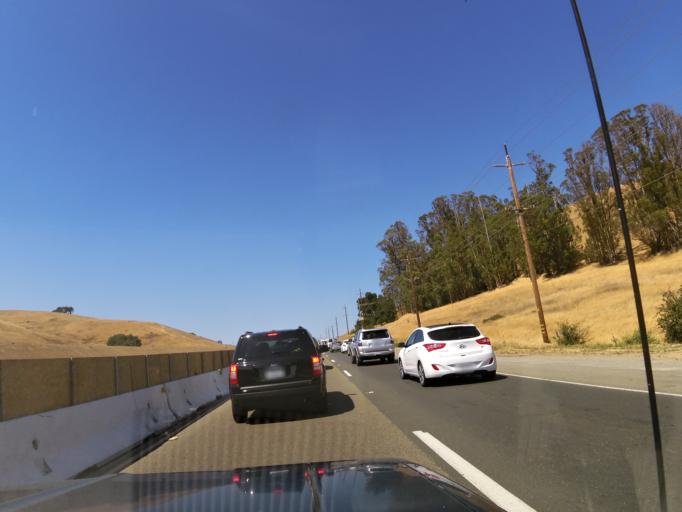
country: US
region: California
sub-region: Sonoma County
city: Petaluma
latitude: 38.1925
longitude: -122.6004
